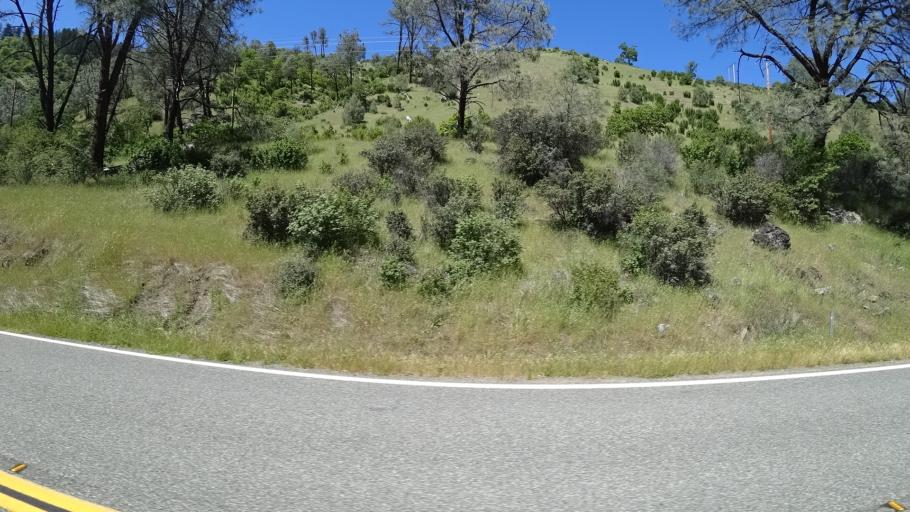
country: US
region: California
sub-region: Trinity County
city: Hayfork
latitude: 40.7412
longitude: -123.2178
